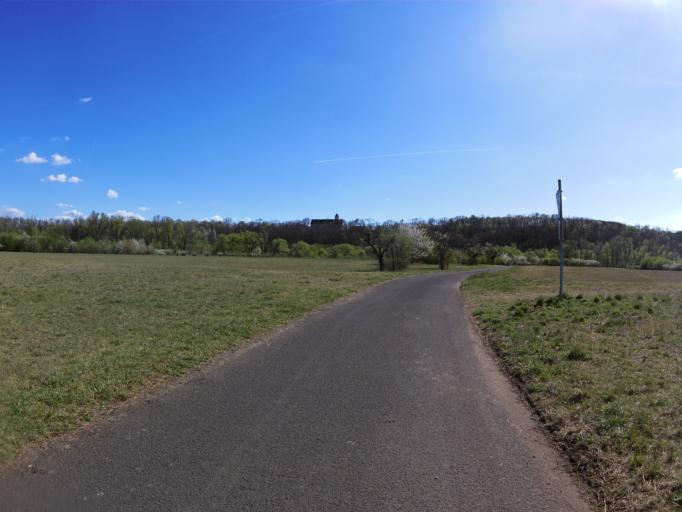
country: DE
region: Bavaria
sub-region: Regierungsbezirk Unterfranken
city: Volkach
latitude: 49.8574
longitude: 10.2117
